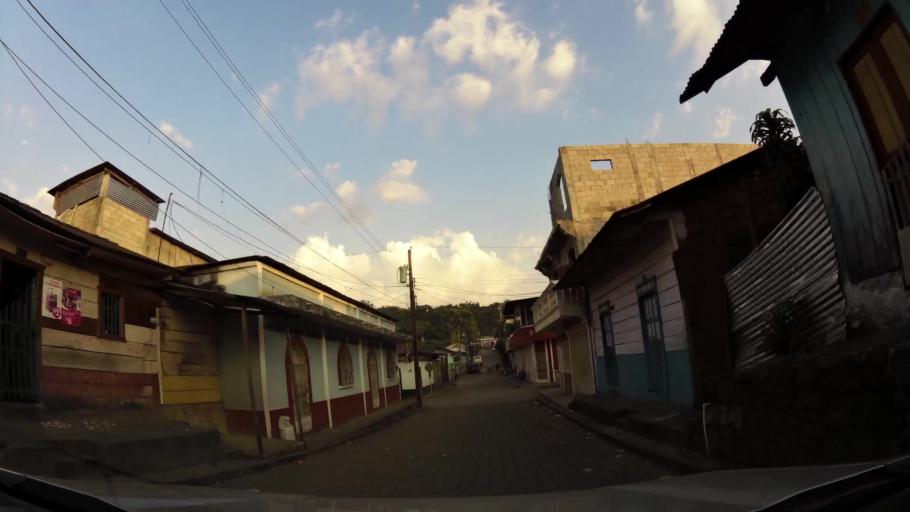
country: GT
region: Retalhuleu
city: San Sebastian
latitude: 14.5602
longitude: -91.6468
